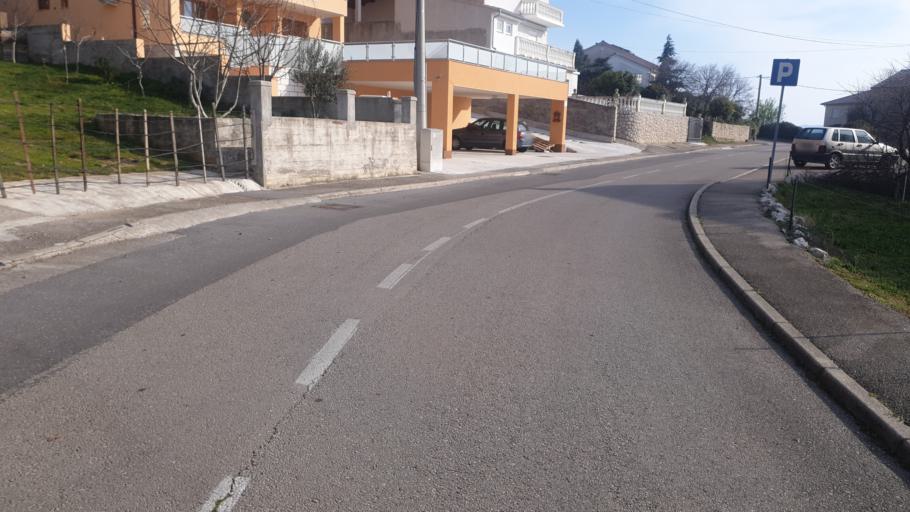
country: HR
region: Primorsko-Goranska
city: Novi Vinodolski
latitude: 45.1306
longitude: 14.7945
